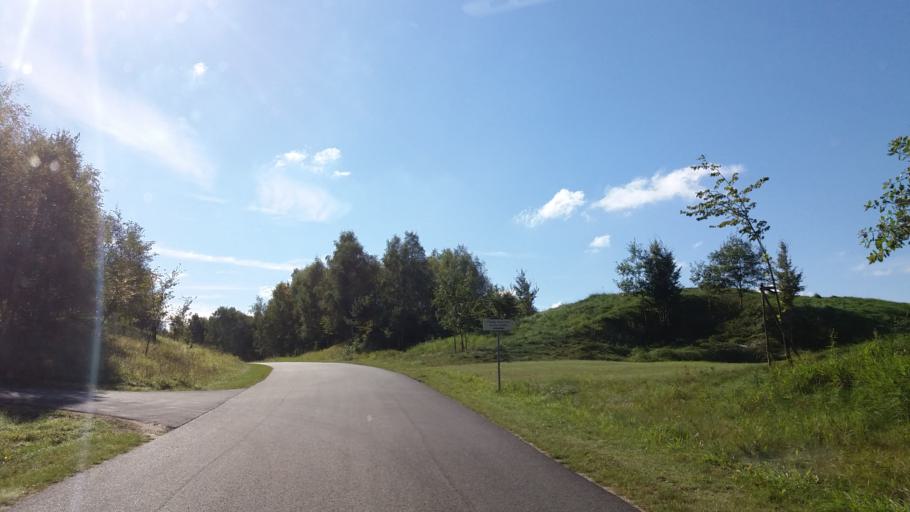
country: PL
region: West Pomeranian Voivodeship
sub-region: Powiat choszczenski
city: Krzecin
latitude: 53.1375
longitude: 15.4794
